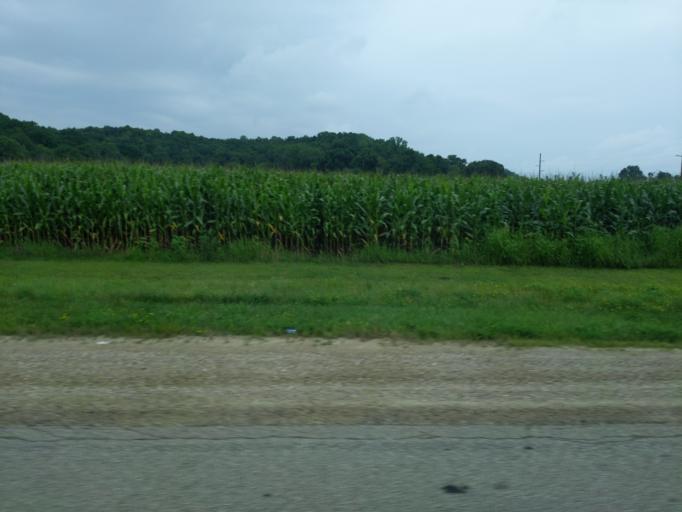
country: US
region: Wisconsin
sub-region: Dane County
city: Mazomanie
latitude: 43.1687
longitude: -89.7730
